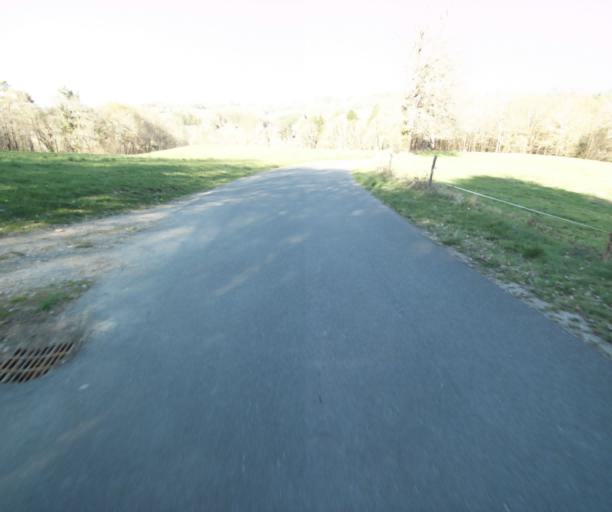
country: FR
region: Limousin
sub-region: Departement de la Correze
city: Tulle
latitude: 45.2856
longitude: 1.7222
